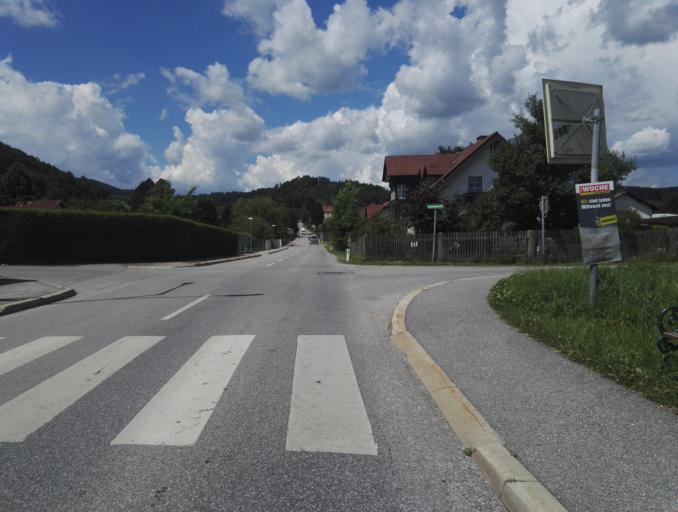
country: AT
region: Styria
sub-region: Politischer Bezirk Graz-Umgebung
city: Gratwein
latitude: 47.1113
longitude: 15.3308
